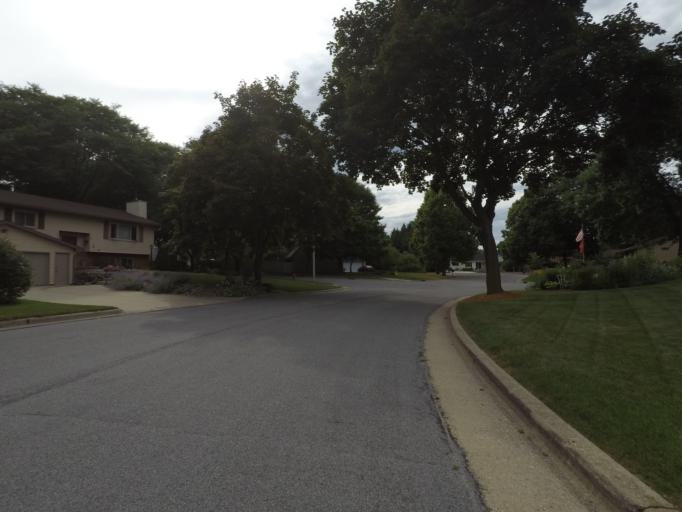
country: US
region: Wisconsin
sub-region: Dane County
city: Middleton
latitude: 43.0761
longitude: -89.4988
